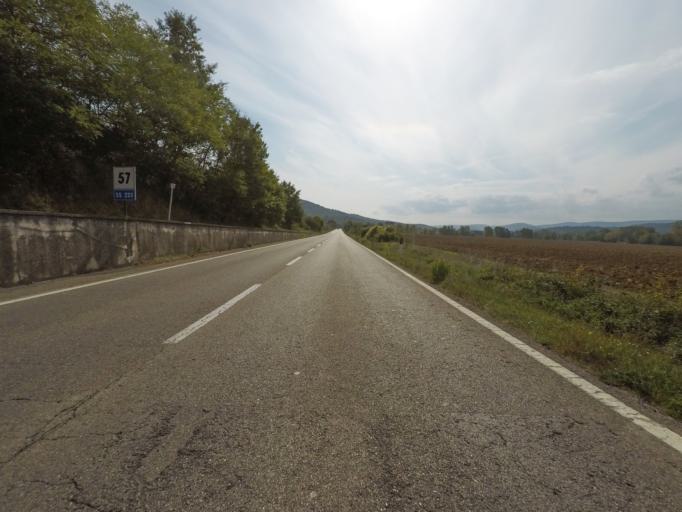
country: IT
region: Tuscany
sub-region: Provincia di Siena
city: Rosia
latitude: 43.2149
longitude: 11.2768
